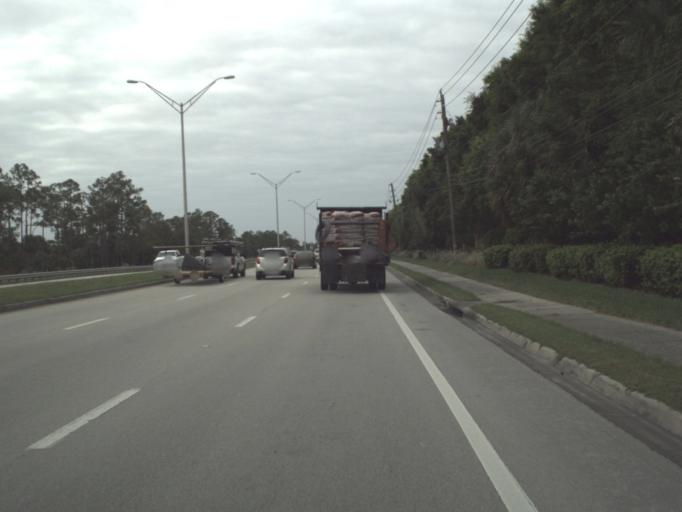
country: US
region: Florida
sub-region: Collier County
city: Lely Resort
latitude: 26.0836
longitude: -81.6875
